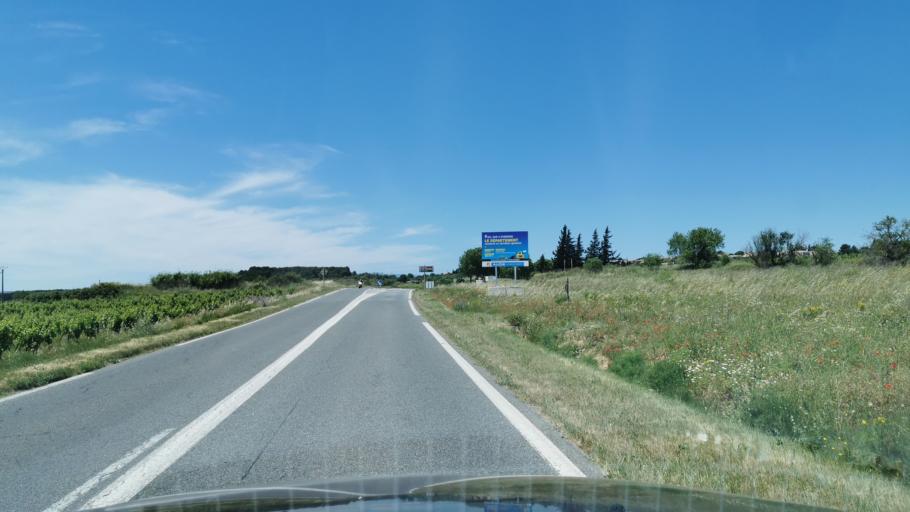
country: FR
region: Languedoc-Roussillon
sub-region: Departement de l'Aude
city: Marcorignan
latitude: 43.2162
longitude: 2.9308
